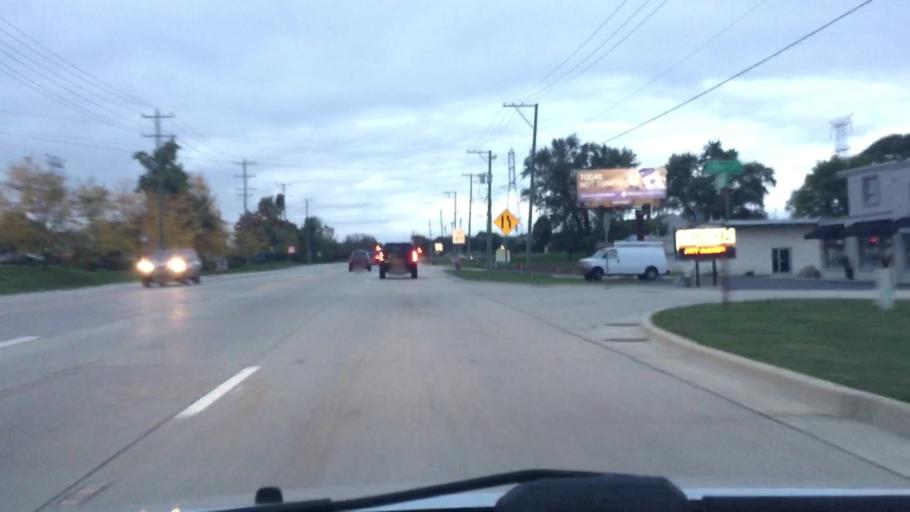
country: US
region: Illinois
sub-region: McHenry County
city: Crystal Lake
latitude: 42.2532
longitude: -88.2866
